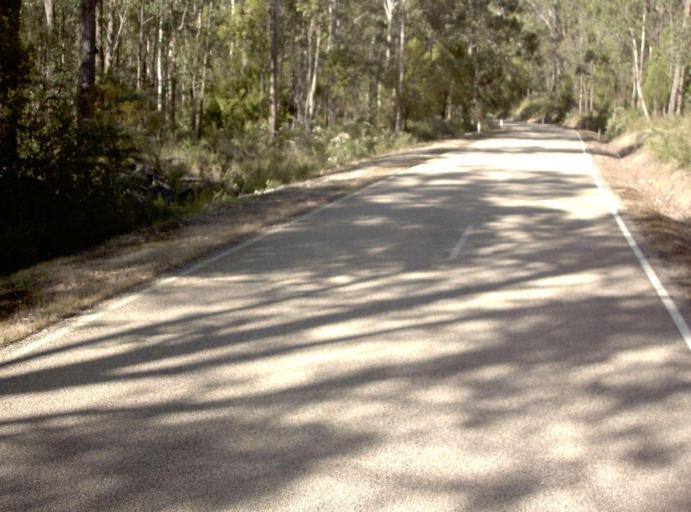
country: AU
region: Victoria
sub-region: East Gippsland
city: Lakes Entrance
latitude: -37.5575
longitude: 148.5570
